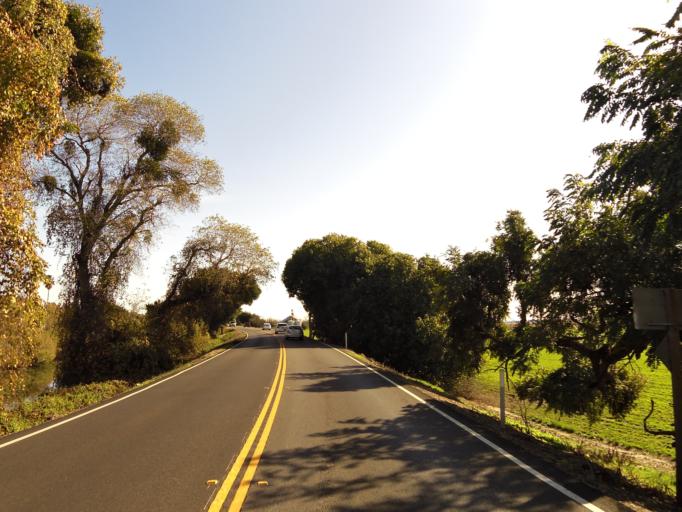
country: US
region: California
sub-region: Solano County
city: Rio Vista
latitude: 38.1700
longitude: -121.6417
